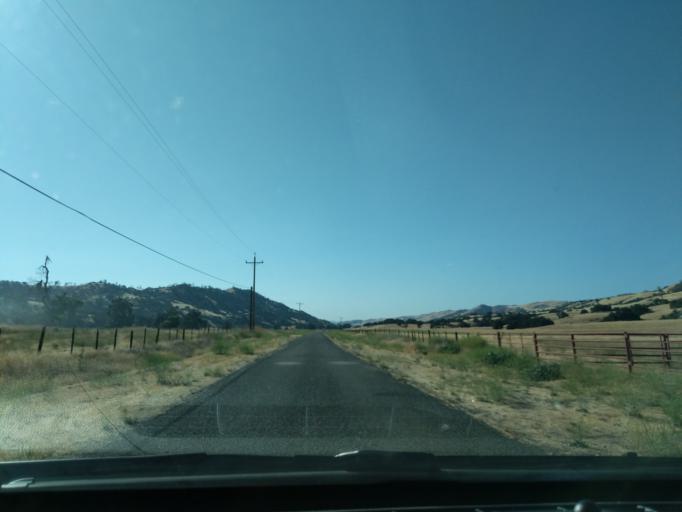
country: US
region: California
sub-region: San Luis Obispo County
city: San Miguel
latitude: 36.1198
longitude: -120.7322
